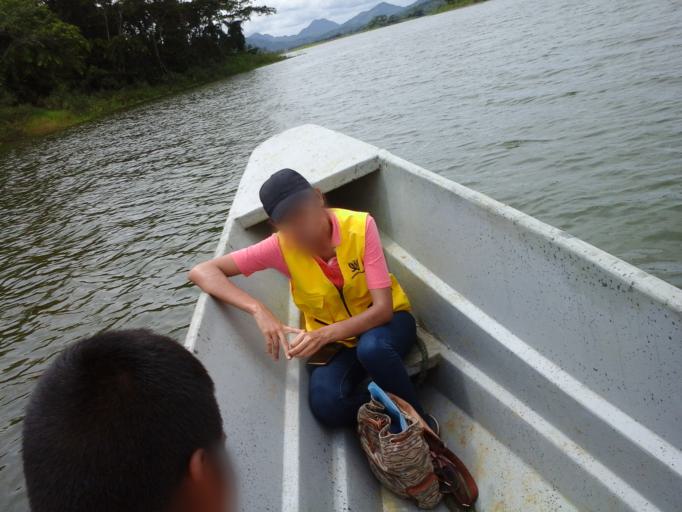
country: CO
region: Bolivar
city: San Cristobal
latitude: 9.8739
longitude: -75.3010
